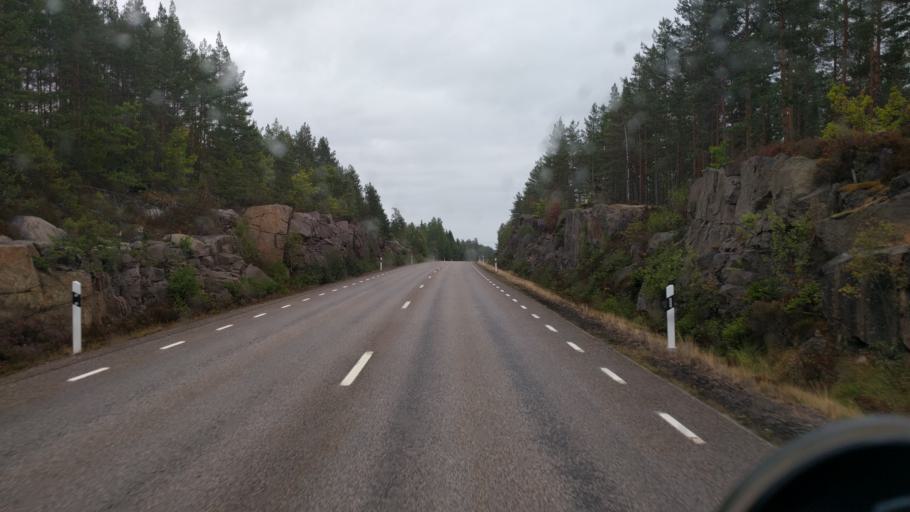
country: SE
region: Kalmar
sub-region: Vasterviks Kommun
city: Ankarsrum
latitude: 57.7009
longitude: 16.2424
